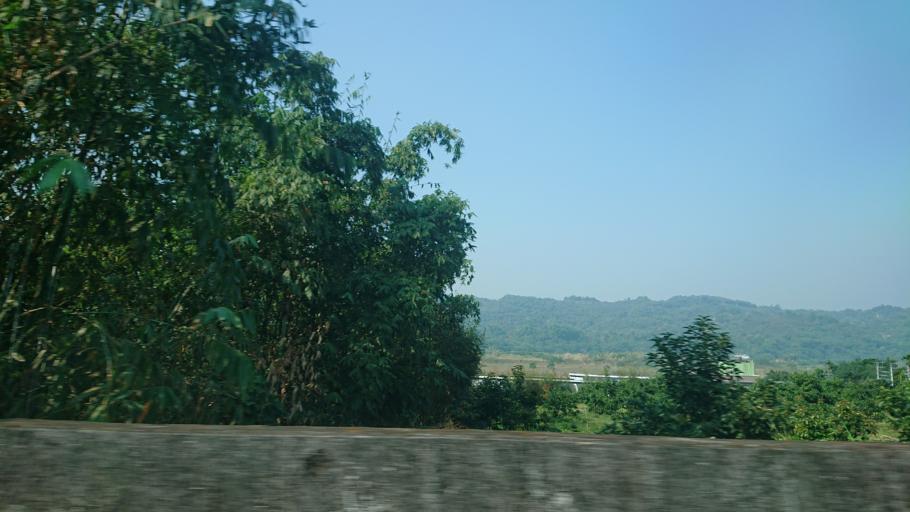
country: TW
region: Taiwan
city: Lugu
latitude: 23.6903
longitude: 120.6634
